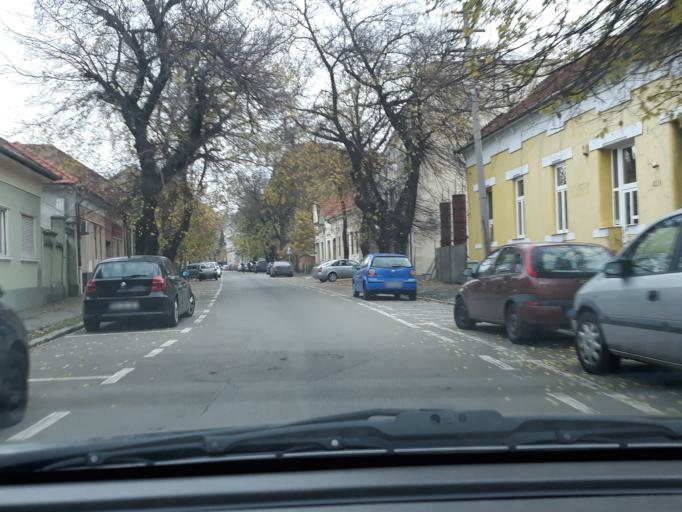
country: RO
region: Bihor
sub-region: Comuna Biharea
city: Oradea
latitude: 47.0632
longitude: 21.9291
